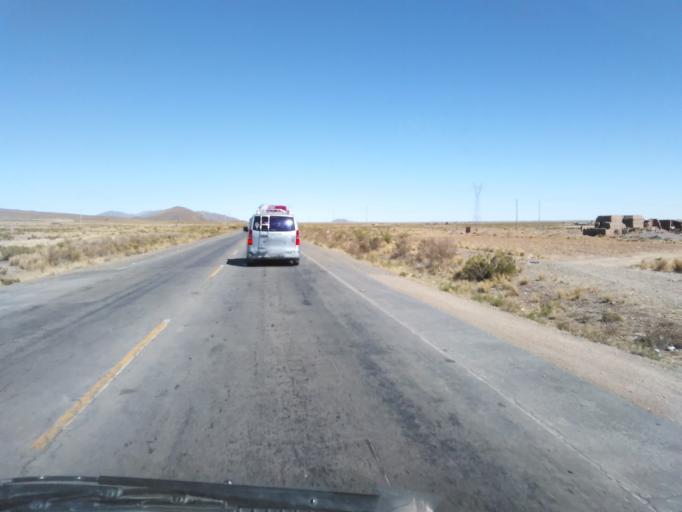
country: BO
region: Oruro
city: Machacamarca
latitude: -18.0697
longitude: -67.0057
